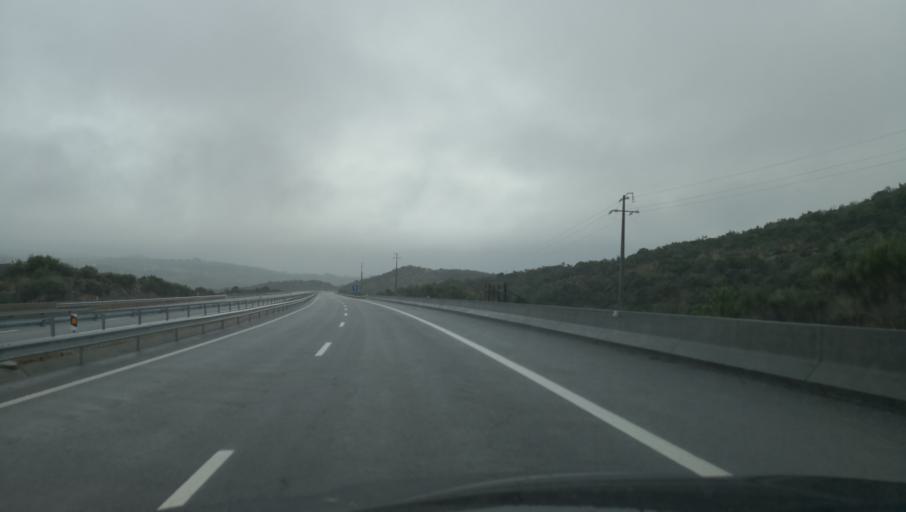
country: PT
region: Vila Real
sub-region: Vila Real
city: Vila Real
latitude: 41.3821
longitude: -7.6653
